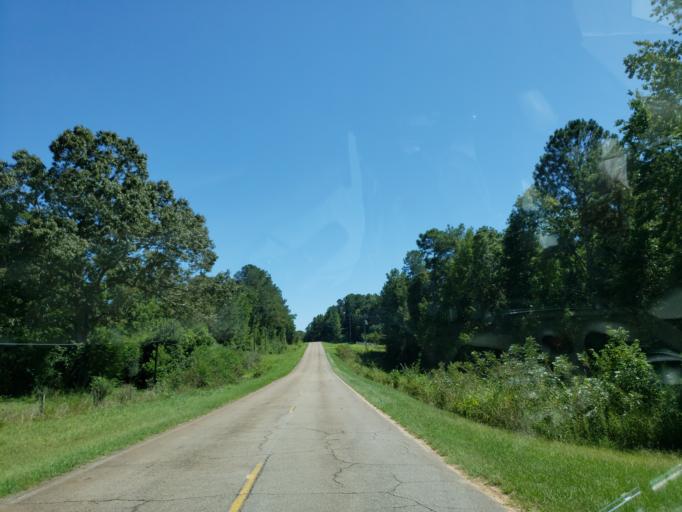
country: US
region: Georgia
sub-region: Crawford County
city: Roberta
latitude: 32.8260
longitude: -84.0702
